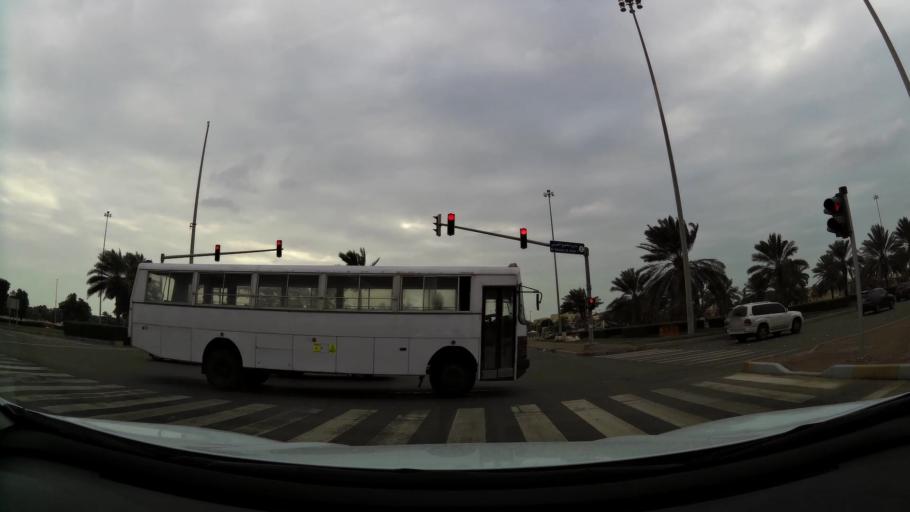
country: AE
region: Abu Dhabi
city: Abu Dhabi
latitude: 24.4353
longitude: 54.3770
